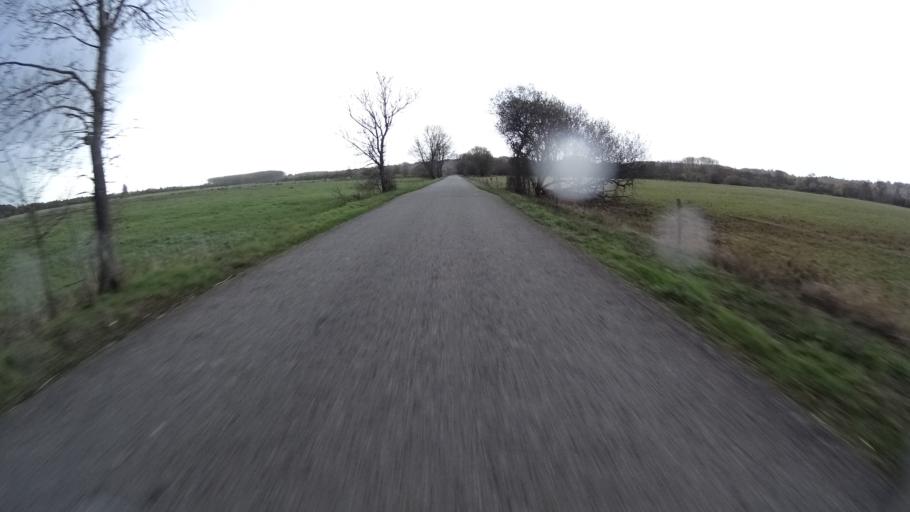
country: FR
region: Brittany
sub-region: Departement d'Ille-et-Vilaine
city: Sainte-Marie
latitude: 47.6702
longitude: -2.0322
